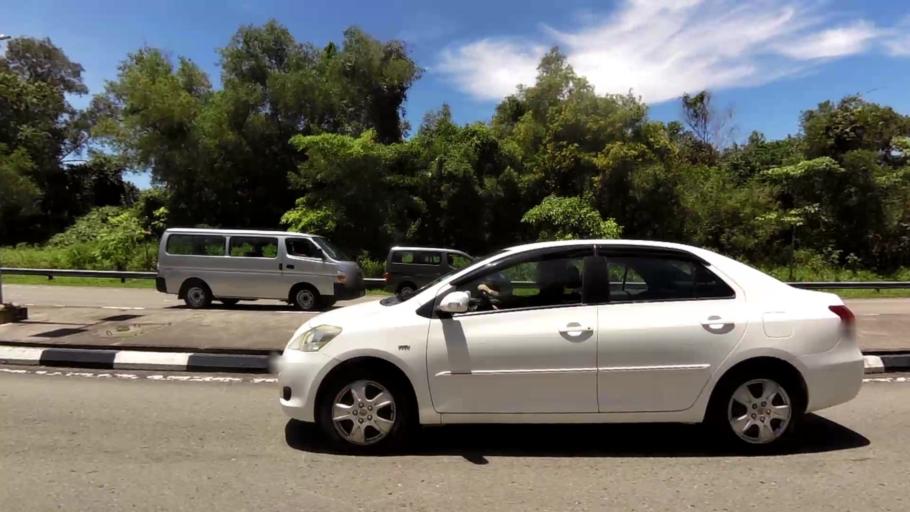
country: BN
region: Brunei and Muara
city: Bandar Seri Begawan
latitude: 4.9203
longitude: 114.9534
